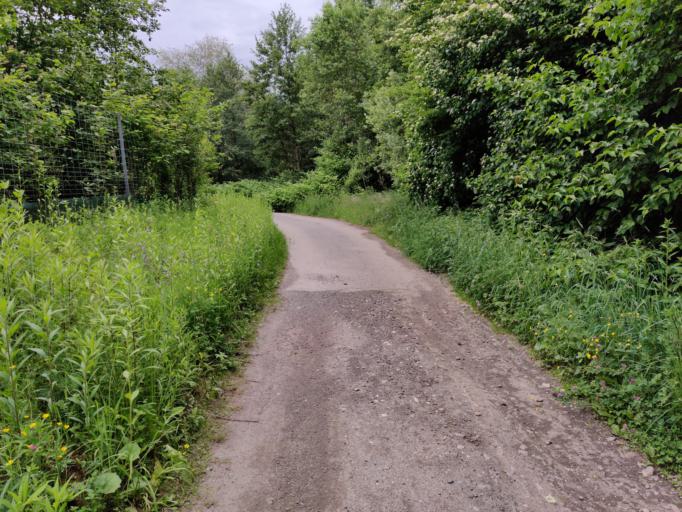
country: AT
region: Carinthia
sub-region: Klagenfurt am Woerthersee
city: Klagenfurt am Woerthersee
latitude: 46.6354
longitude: 14.2468
